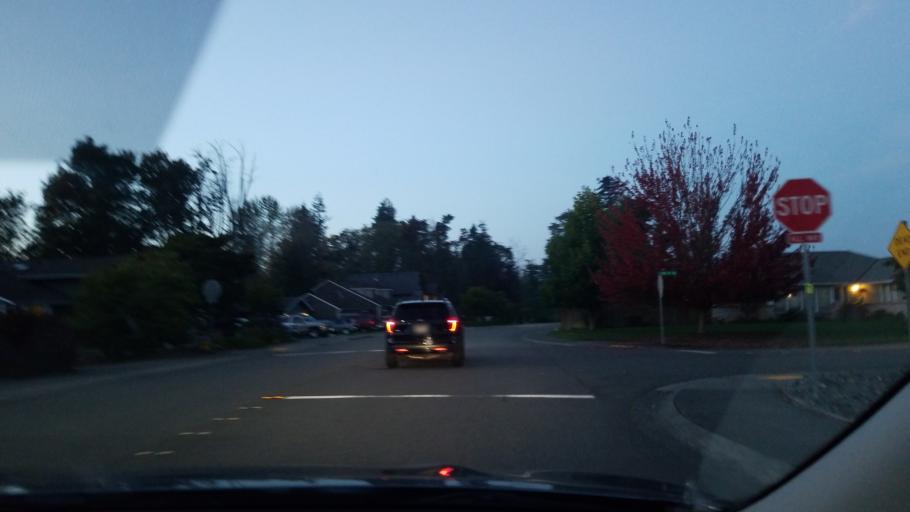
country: US
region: Washington
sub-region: Snohomish County
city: Silver Firs
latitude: 47.8794
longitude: -122.1737
